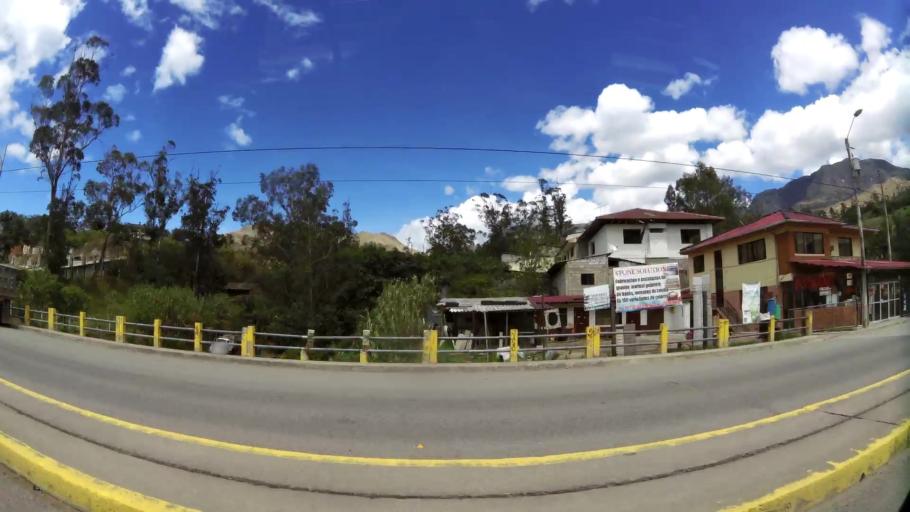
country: EC
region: Azuay
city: Cuenca
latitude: -3.1575
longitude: -79.1485
